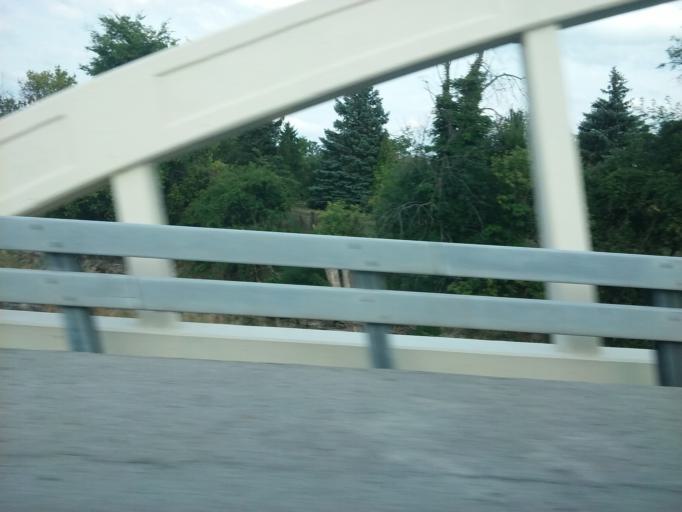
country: US
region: Ohio
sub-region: Wood County
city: Bowling Green
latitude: 41.2988
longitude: -83.6503
